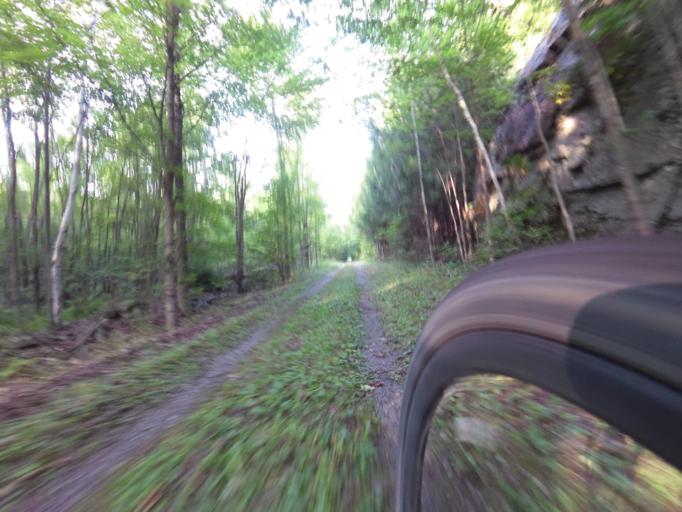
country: CA
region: Ontario
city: Gananoque
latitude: 44.5616
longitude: -76.3648
